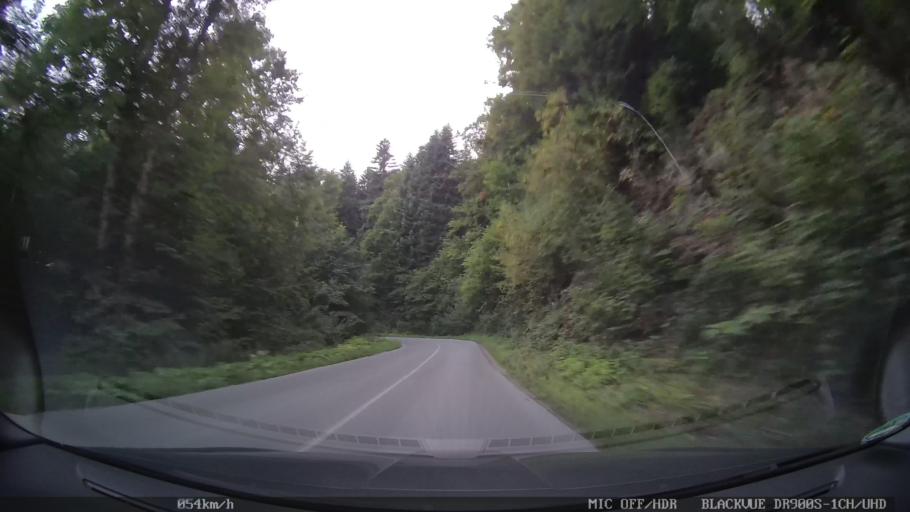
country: HR
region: Primorsko-Goranska
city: Vrbovsko
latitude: 45.2017
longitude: 15.0260
